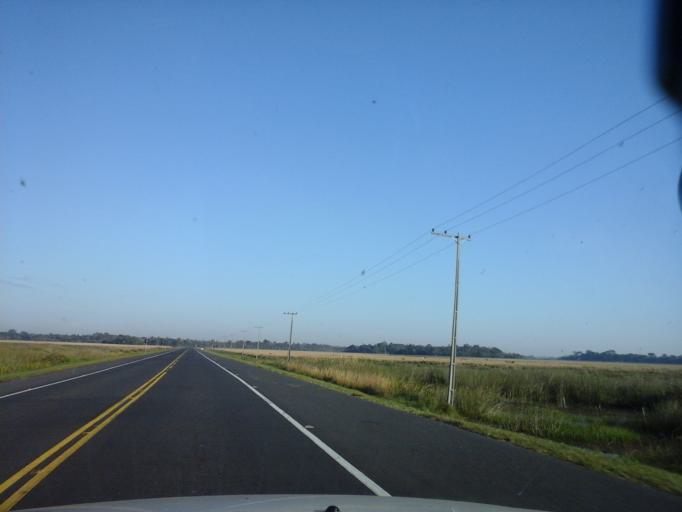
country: PY
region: Neembucu
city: Pilar
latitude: -26.8619
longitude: -57.9460
